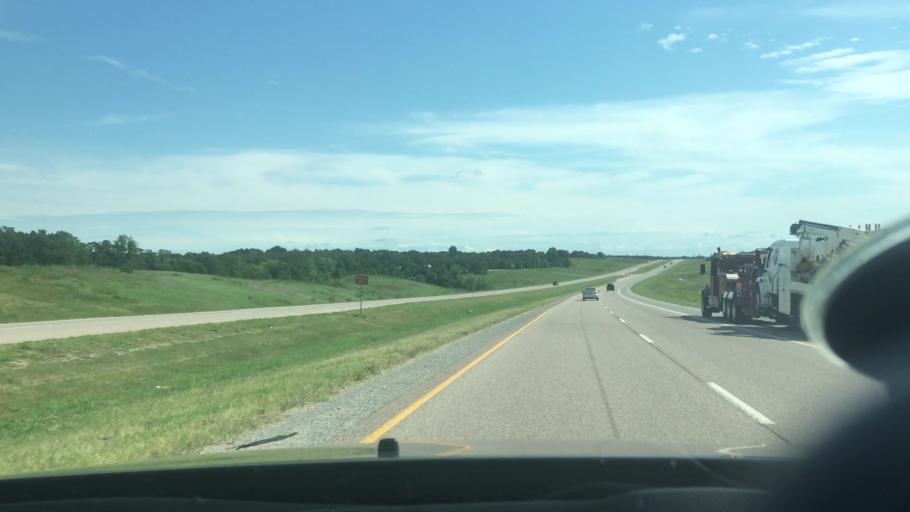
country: US
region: Oklahoma
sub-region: Pontotoc County
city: Byng
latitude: 34.8894
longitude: -96.6753
